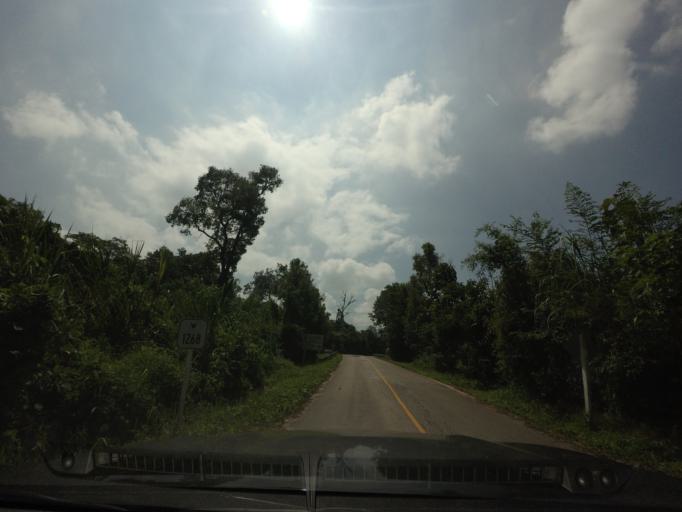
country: TH
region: Loei
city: Na Haeo
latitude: 17.4763
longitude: 100.9398
